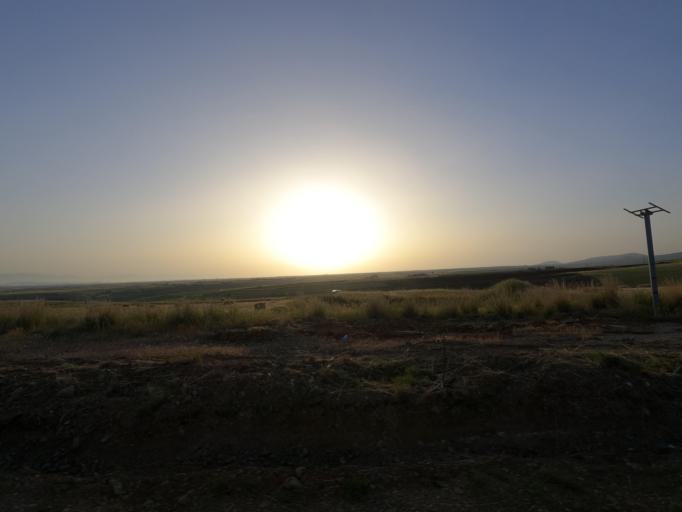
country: CY
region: Lefkosia
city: Astromeritis
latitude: 35.1057
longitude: 33.0149
